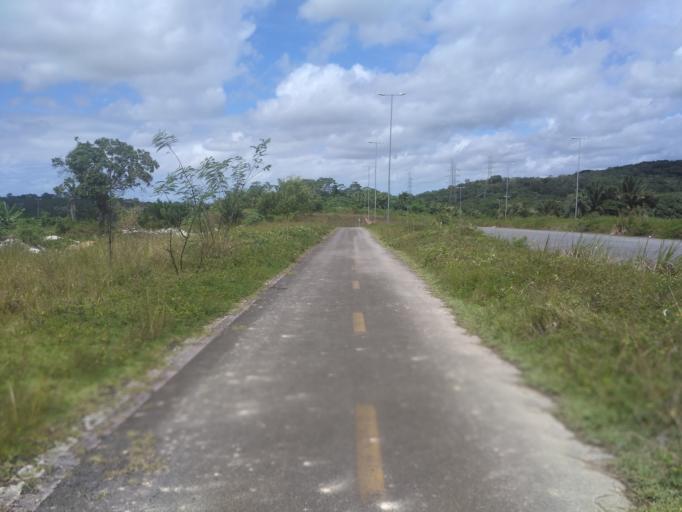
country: BR
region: Pernambuco
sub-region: Sao Lourenco Da Mata
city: Sao Lourenco da Mata
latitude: -8.0409
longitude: -34.9980
